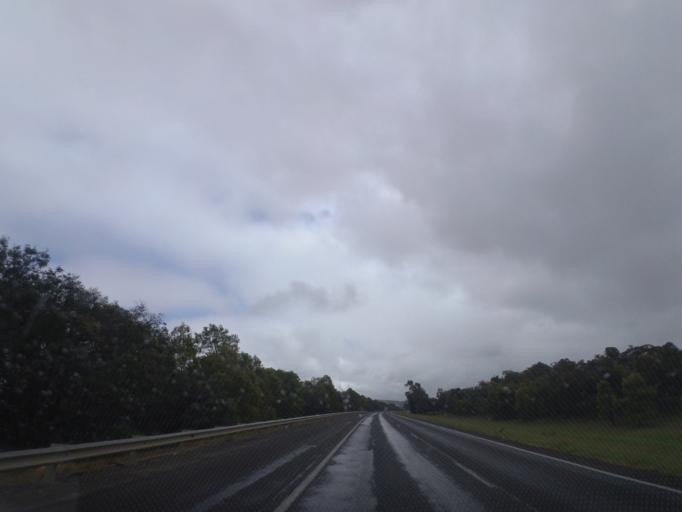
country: AU
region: Victoria
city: Black Hill
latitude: -37.5345
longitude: 143.8754
